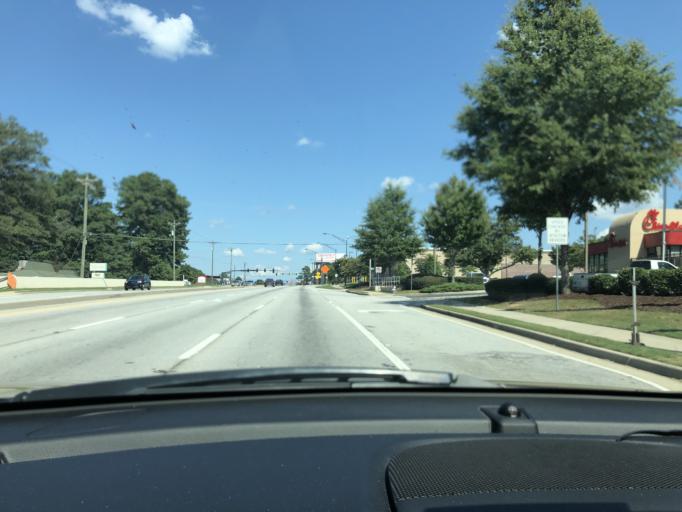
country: US
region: Georgia
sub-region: Gwinnett County
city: Snellville
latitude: 33.8532
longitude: -84.0360
